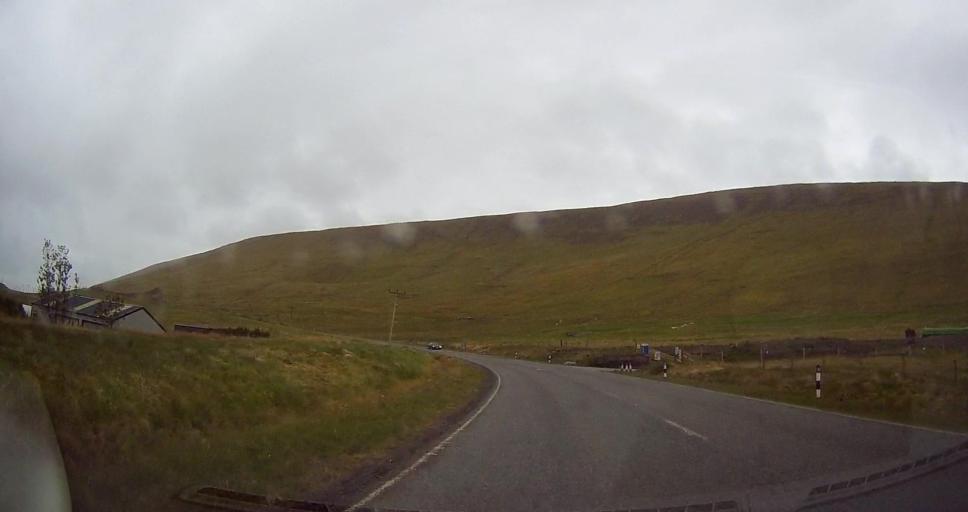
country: GB
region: Scotland
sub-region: Shetland Islands
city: Lerwick
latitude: 60.2544
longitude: -1.2950
